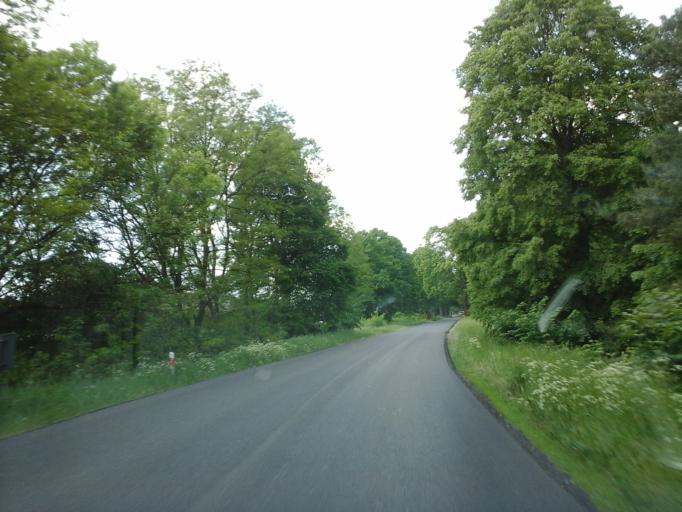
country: PL
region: West Pomeranian Voivodeship
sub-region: Powiat choszczenski
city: Recz
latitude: 53.1899
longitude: 15.6369
